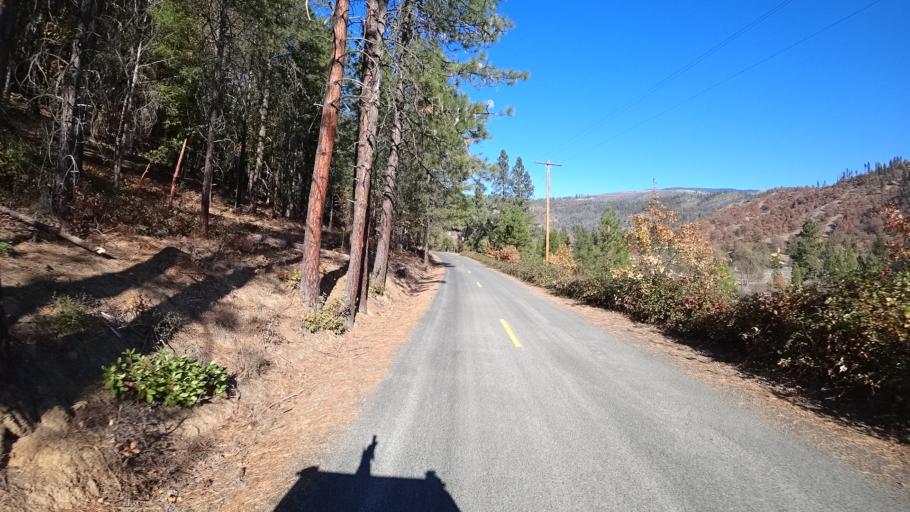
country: US
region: California
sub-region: Siskiyou County
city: Yreka
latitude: 41.8240
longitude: -122.9762
